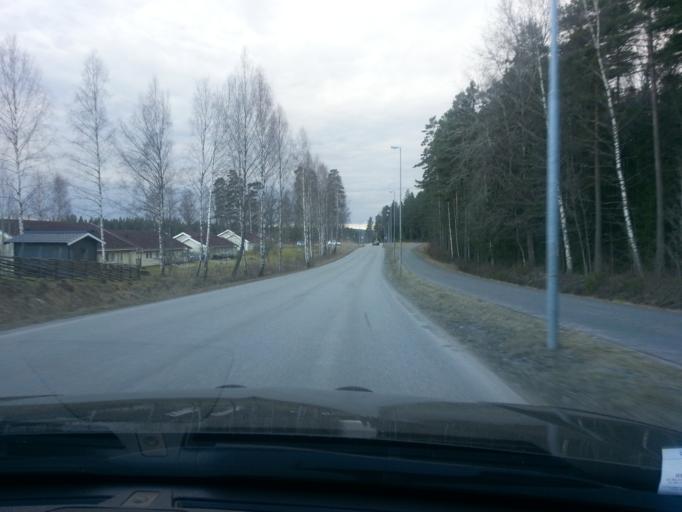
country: SE
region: Joenkoeping
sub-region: Vetlanda Kommun
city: Vetlanda
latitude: 57.4115
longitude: 15.0579
